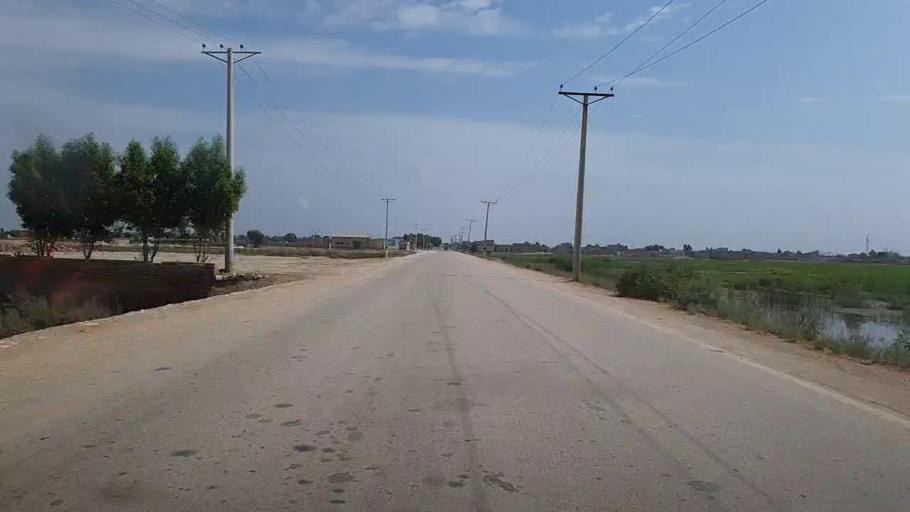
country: PK
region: Sindh
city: Thul
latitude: 28.2508
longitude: 68.7821
